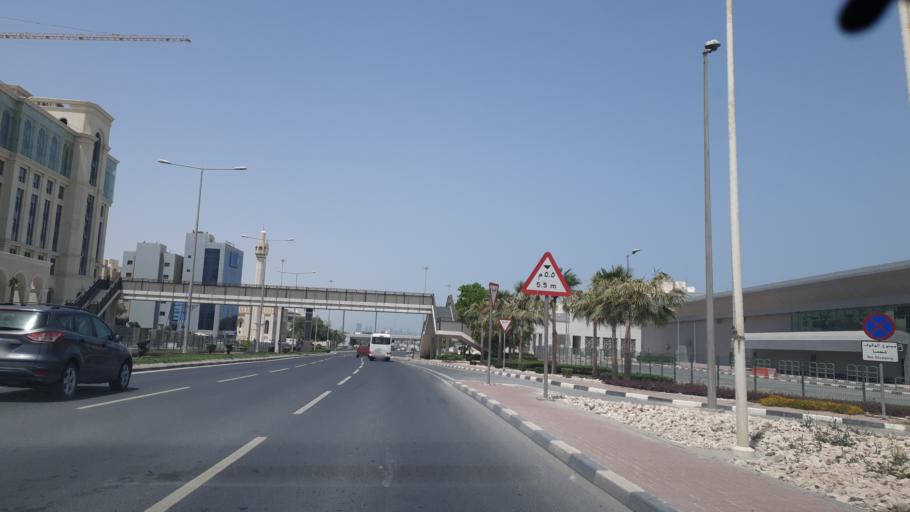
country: QA
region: Baladiyat ad Dawhah
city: Doha
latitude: 25.2796
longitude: 51.5522
